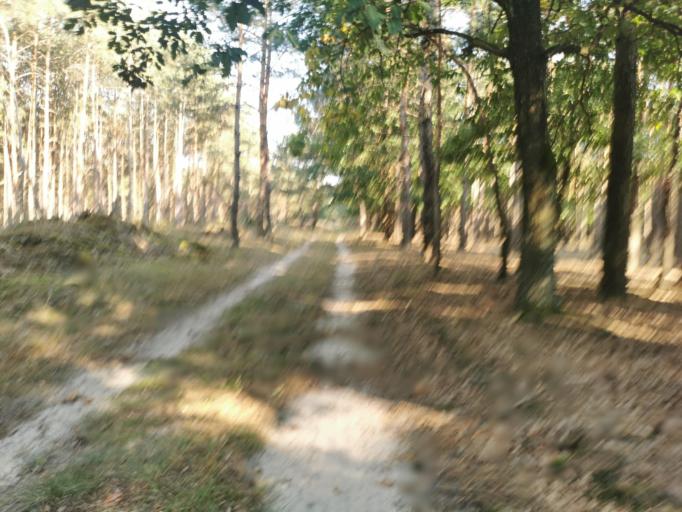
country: SK
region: Trnavsky
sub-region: Okres Senica
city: Senica
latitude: 48.6435
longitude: 17.2915
